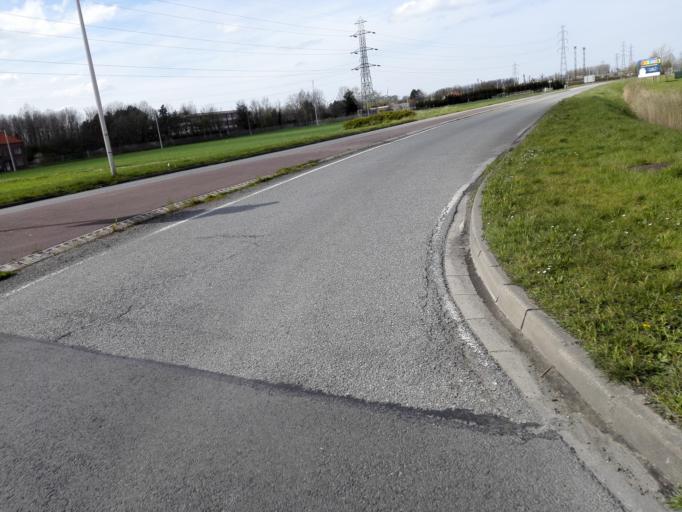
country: FR
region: Nord-Pas-de-Calais
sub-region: Departement du Nord
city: Grande-Synthe
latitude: 50.9928
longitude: 2.2964
